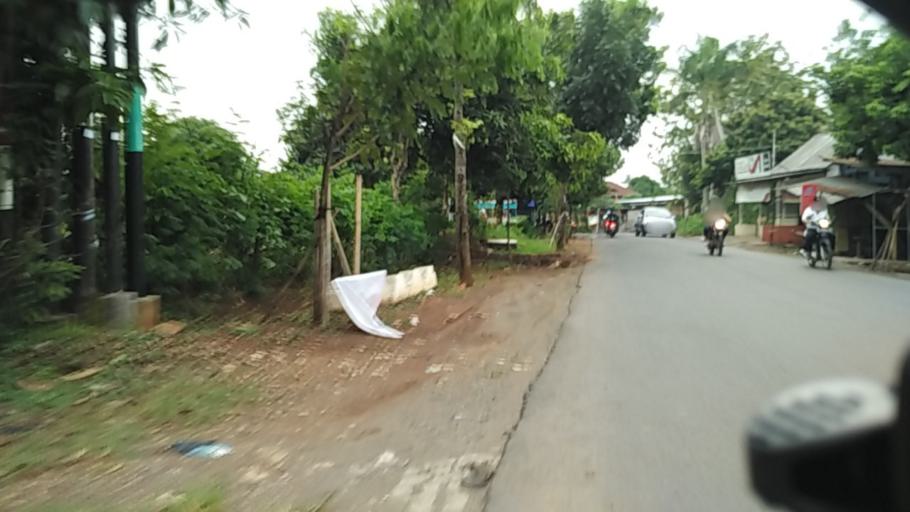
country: ID
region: Central Java
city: Semarang
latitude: -7.0679
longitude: 110.4320
